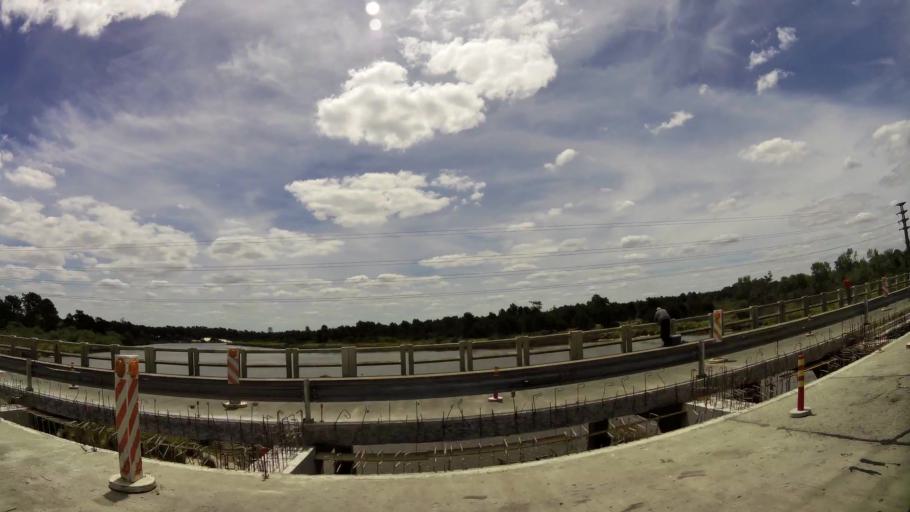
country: UY
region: Canelones
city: Empalme Olmos
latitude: -34.7861
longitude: -55.8906
